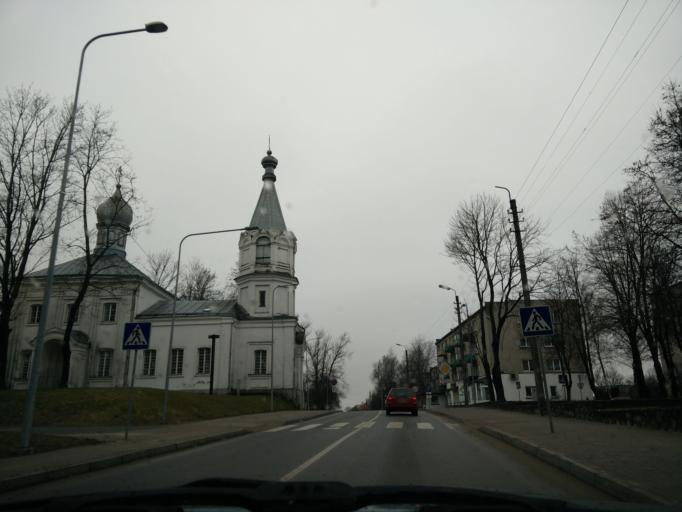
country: LT
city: Raseiniai
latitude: 55.3839
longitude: 23.1203
